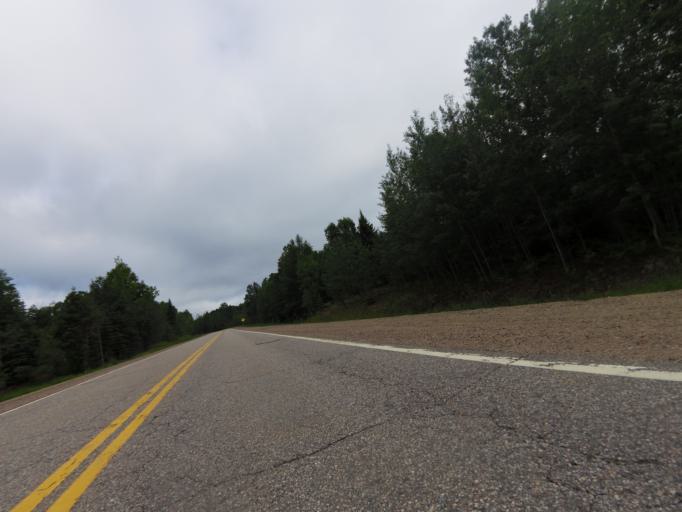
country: CA
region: Quebec
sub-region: Outaouais
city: Shawville
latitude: 45.9097
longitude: -76.3125
